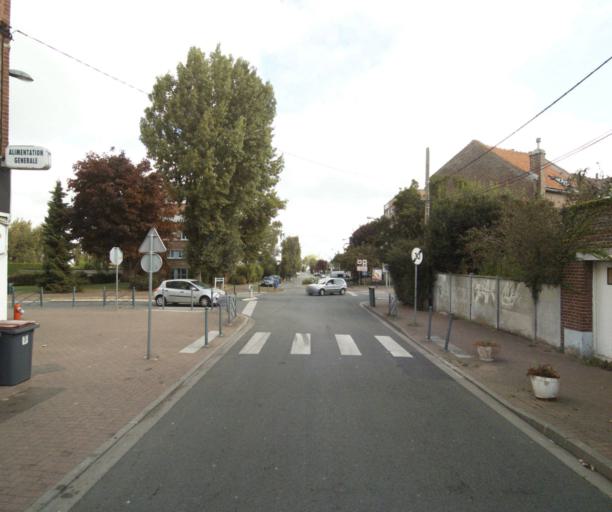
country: FR
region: Nord-Pas-de-Calais
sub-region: Departement du Nord
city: La Madeleine
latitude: 50.6502
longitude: 3.0961
